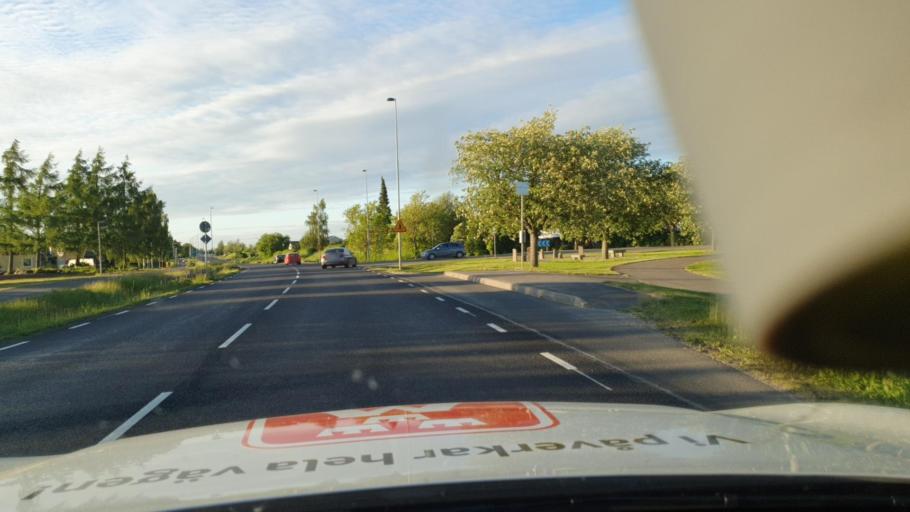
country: SE
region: Vaestra Goetaland
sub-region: Falkopings Kommun
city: Falkoeping
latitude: 58.1547
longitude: 13.5618
